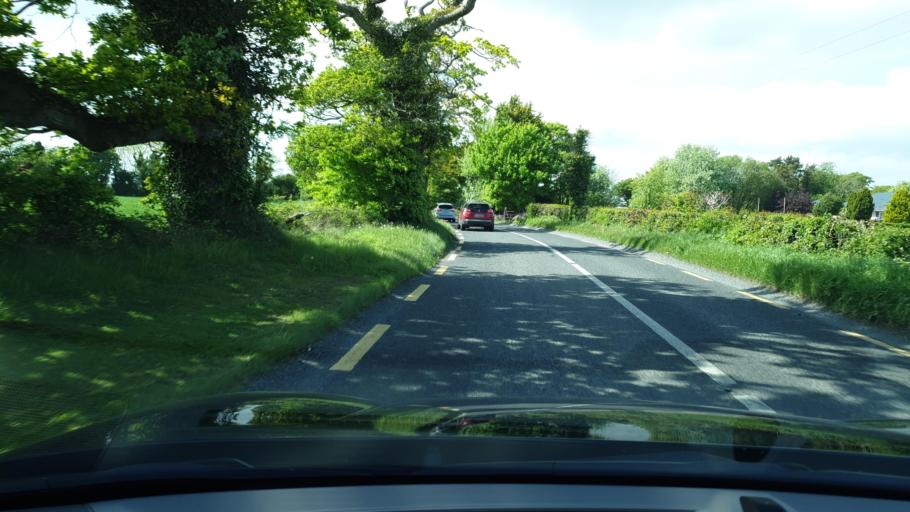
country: IE
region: Leinster
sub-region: An Mhi
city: Dunshaughlin
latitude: 53.5187
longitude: -6.5015
